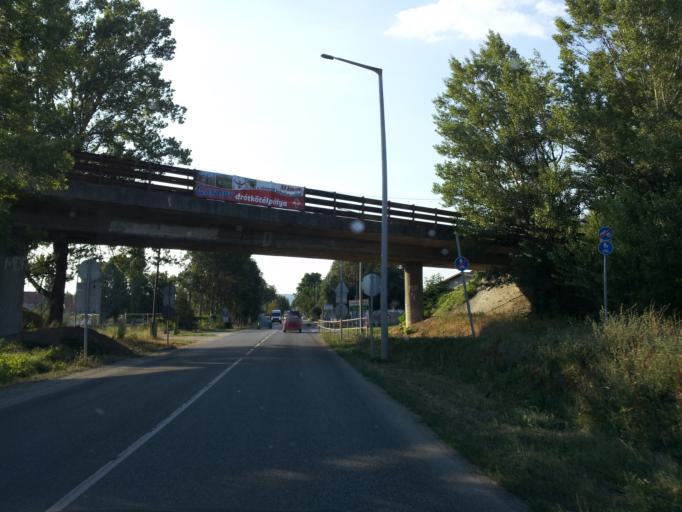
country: HU
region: Pest
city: Dunabogdany
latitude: 47.7884
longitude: 19.0425
